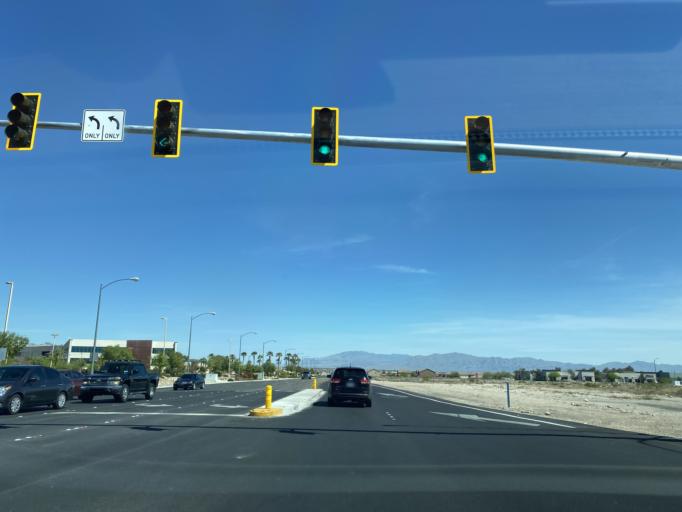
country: US
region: Nevada
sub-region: Clark County
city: Spring Valley
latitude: 36.0702
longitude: -115.2607
